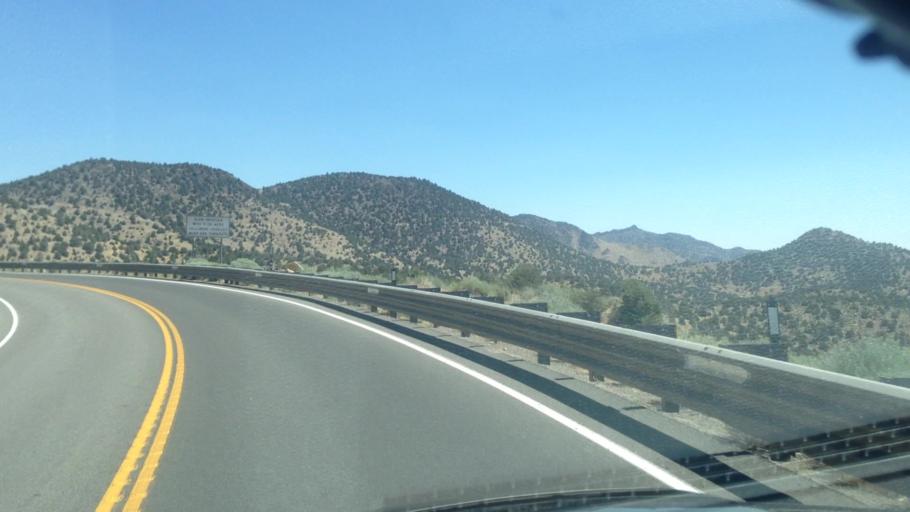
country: US
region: Nevada
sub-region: Storey County
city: Virginia City
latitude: 39.3200
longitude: -119.6435
